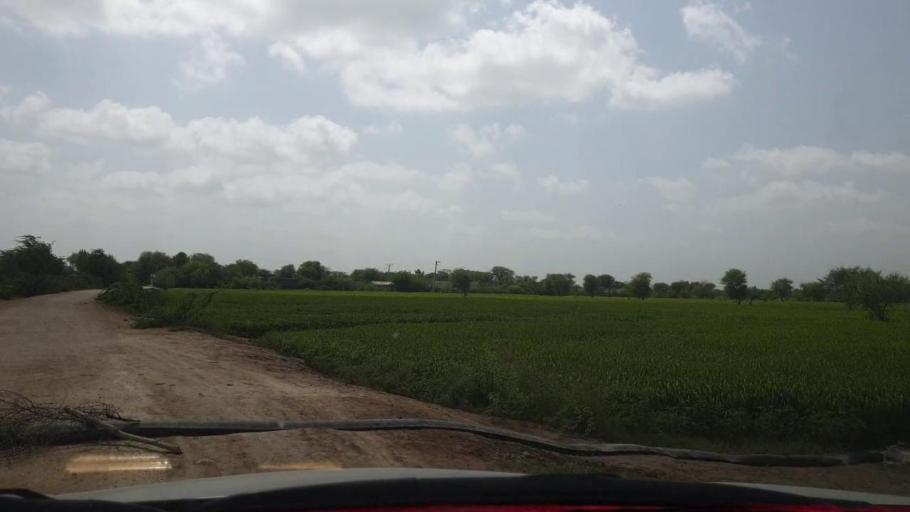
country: PK
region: Sindh
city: Talhar
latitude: 24.9084
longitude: 68.8457
